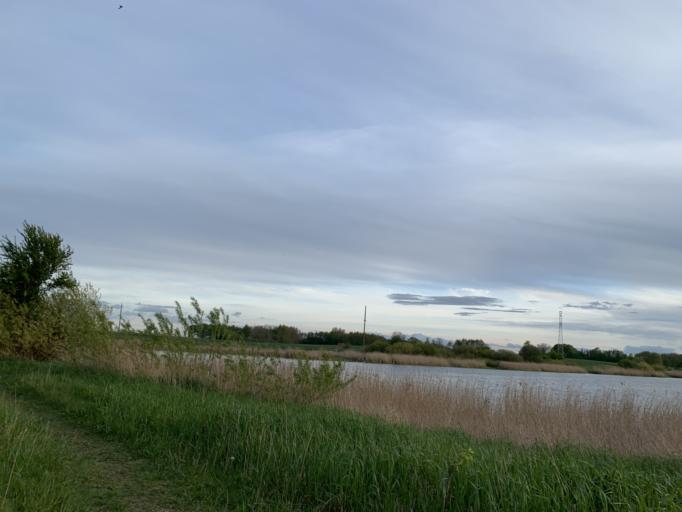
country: BY
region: Minsk
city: Nyasvizh
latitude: 53.2080
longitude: 26.6721
